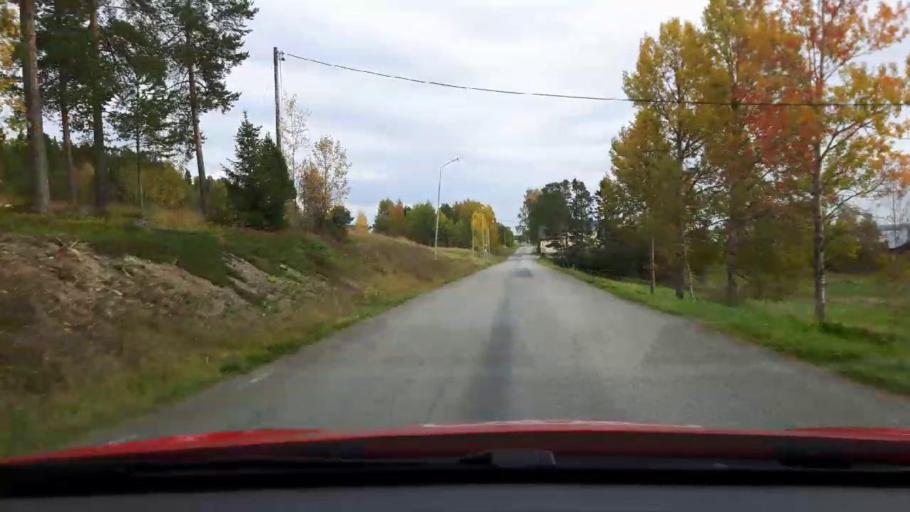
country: SE
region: Jaemtland
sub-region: Krokoms Kommun
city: Valla
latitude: 63.2548
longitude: 14.0252
